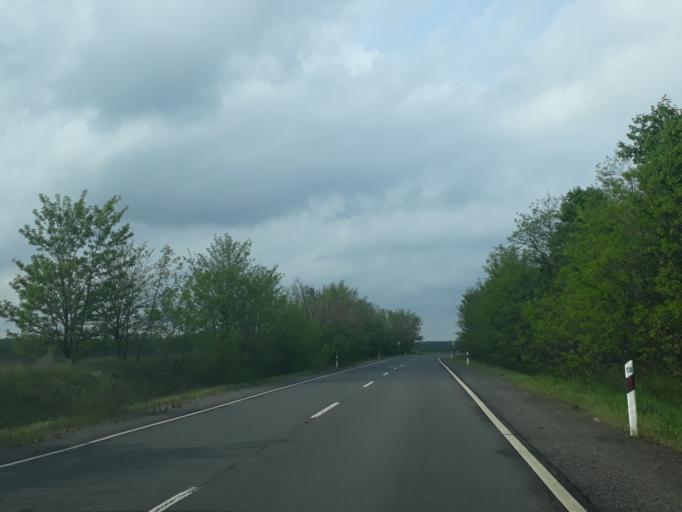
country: HU
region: Szabolcs-Szatmar-Bereg
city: Patroha
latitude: 48.1570
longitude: 22.0278
